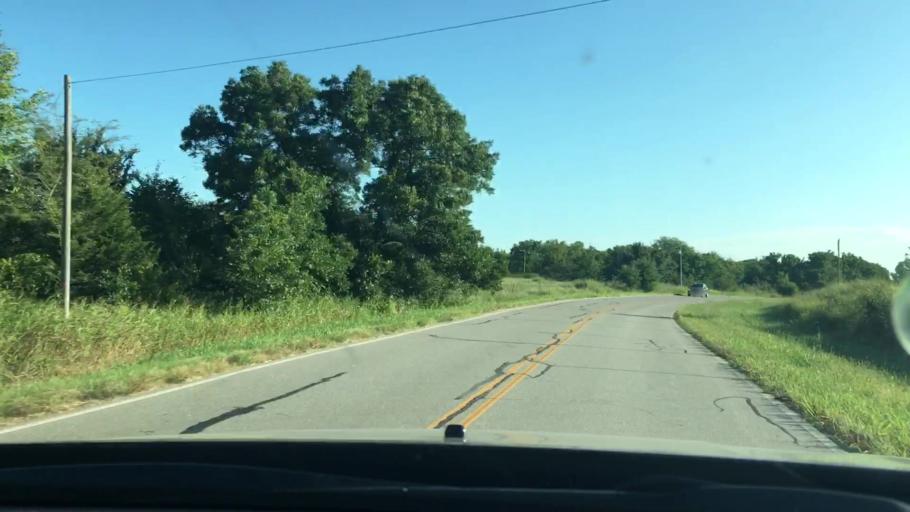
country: US
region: Oklahoma
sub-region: Pontotoc County
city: Ada
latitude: 34.6976
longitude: -96.4410
